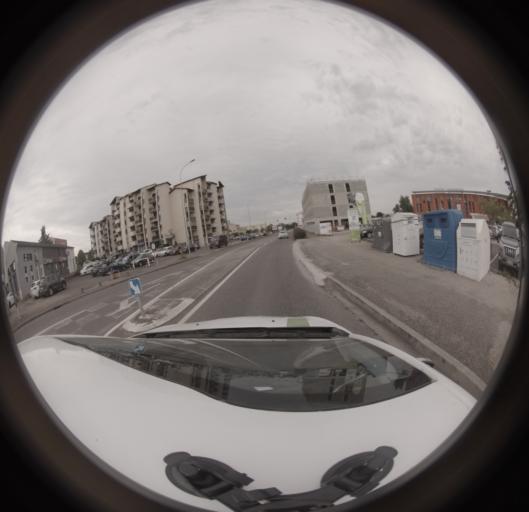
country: FR
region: Midi-Pyrenees
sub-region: Departement du Tarn-et-Garonne
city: Montauban
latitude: 44.0091
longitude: 1.3757
